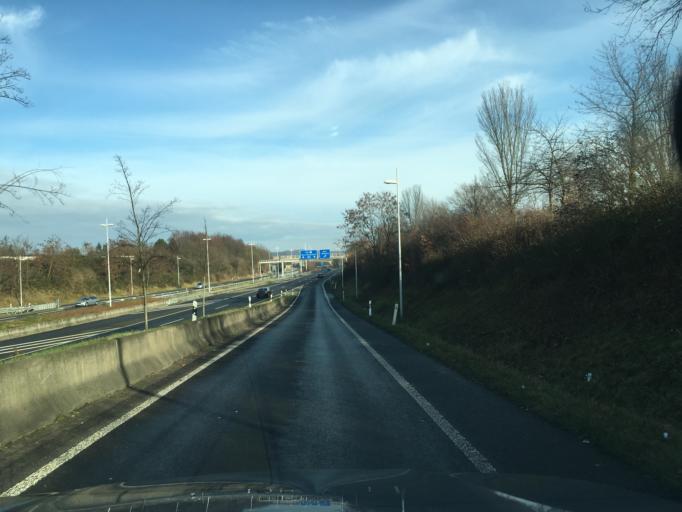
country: DE
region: North Rhine-Westphalia
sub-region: Regierungsbezirk Koln
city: Bonn
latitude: 50.7060
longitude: 7.1335
